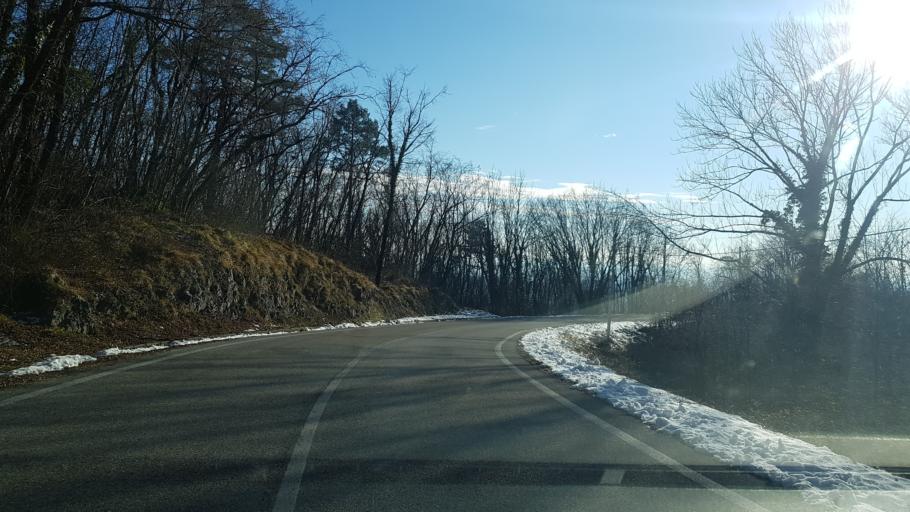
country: IT
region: Friuli Venezia Giulia
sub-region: Provincia di Udine
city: Forgaria nel Friuli
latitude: 46.2371
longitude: 12.9922
